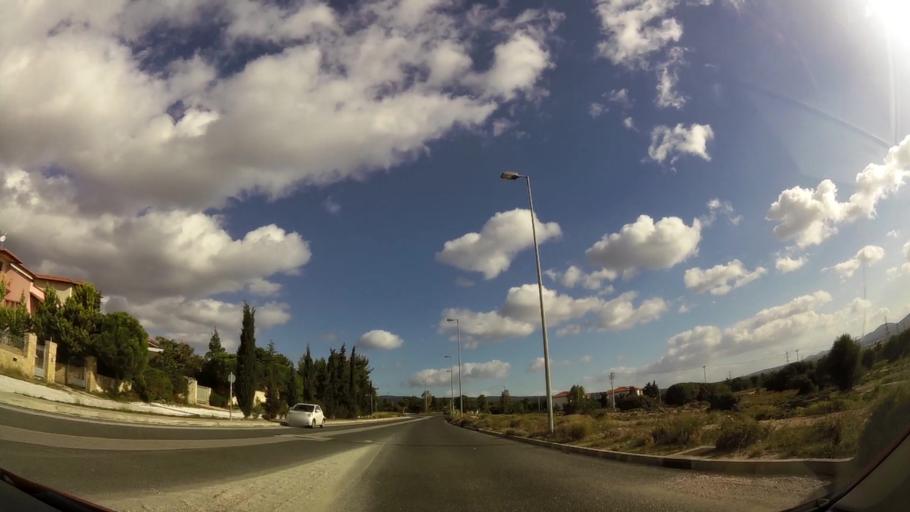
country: GR
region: Attica
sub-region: Nomarchia Anatolikis Attikis
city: Thrakomakedones
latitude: 38.1200
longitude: 23.7634
